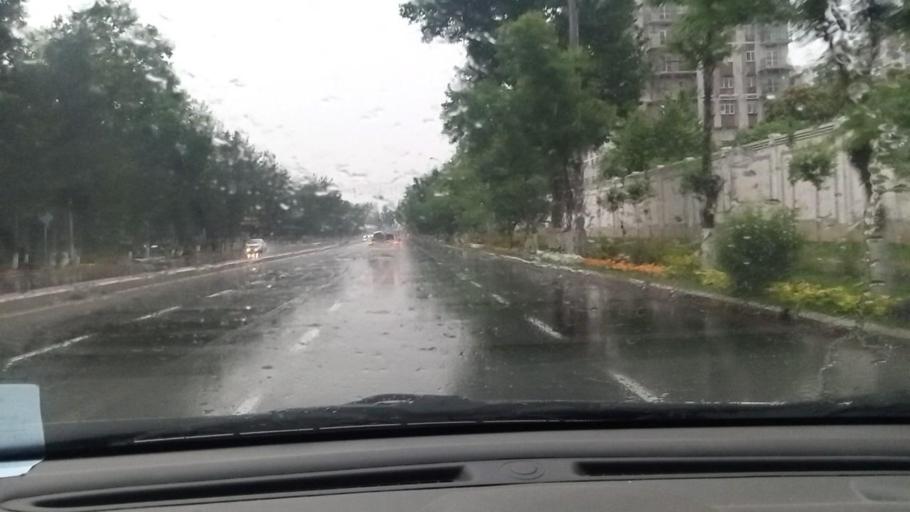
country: UZ
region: Toshkent
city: Salor
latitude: 41.3254
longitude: 69.3607
